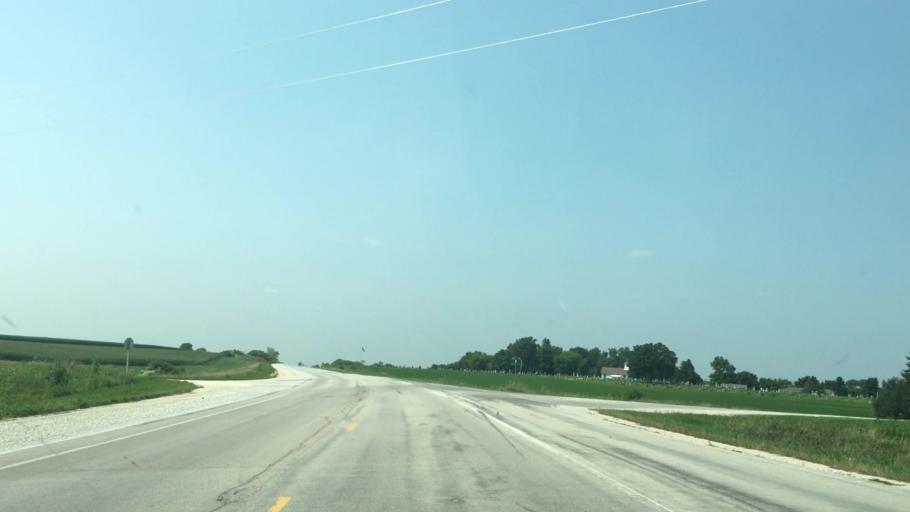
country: US
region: Iowa
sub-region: Winneshiek County
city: Decorah
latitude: 43.4502
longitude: -91.8643
